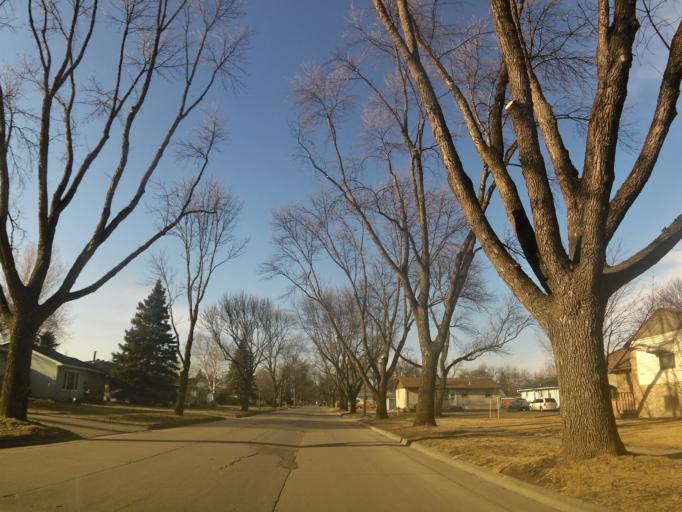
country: US
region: North Dakota
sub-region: Grand Forks County
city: Grand Forks
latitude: 47.9066
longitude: -97.0511
